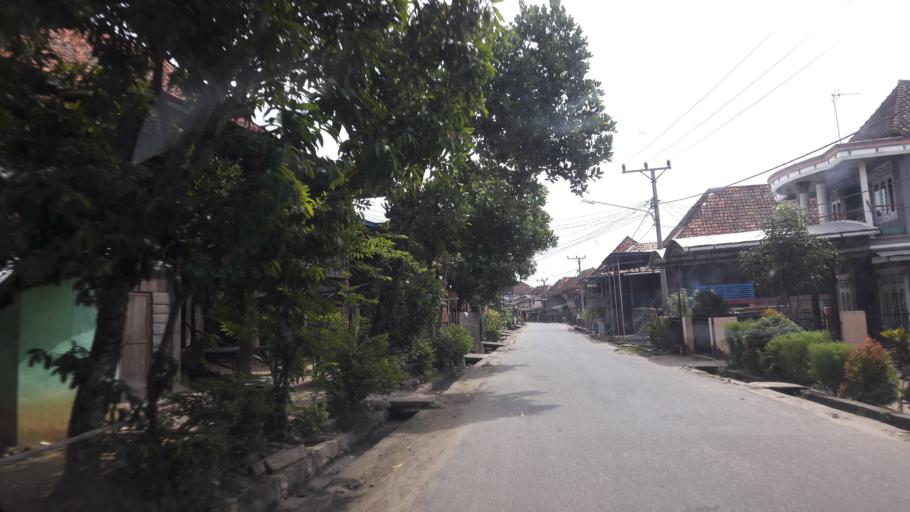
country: ID
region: South Sumatra
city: Gunungmenang
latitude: -3.1512
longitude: 104.1177
